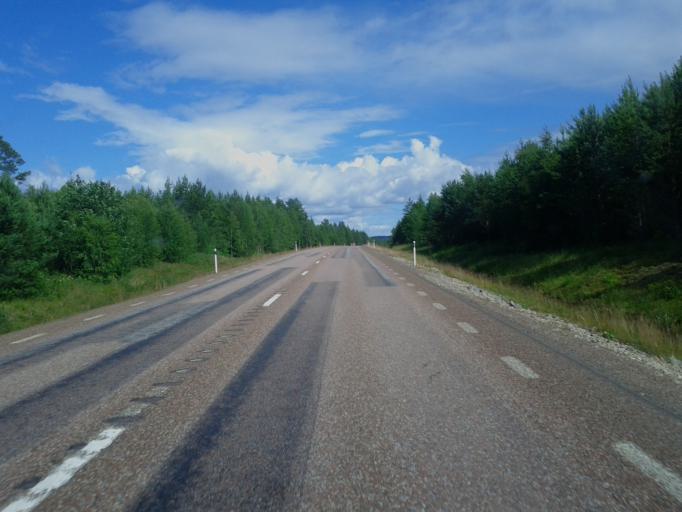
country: SE
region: Dalarna
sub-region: Rattviks Kommun
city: Raettvik
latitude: 60.8448
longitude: 15.1763
